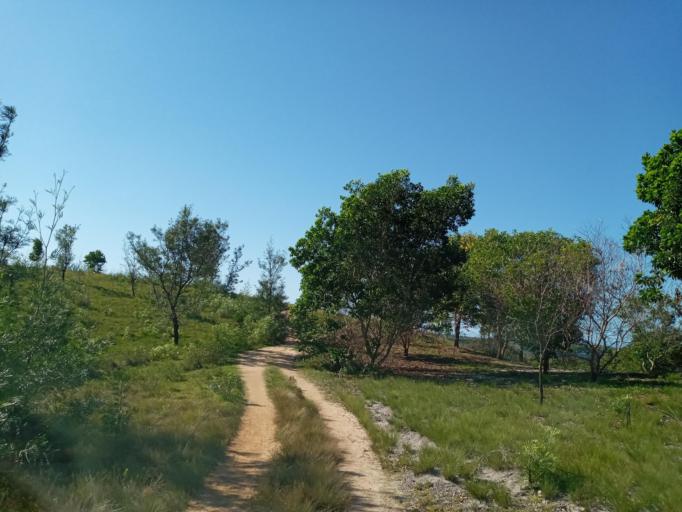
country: MG
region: Anosy
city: Fort Dauphin
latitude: -24.9110
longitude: 47.0902
